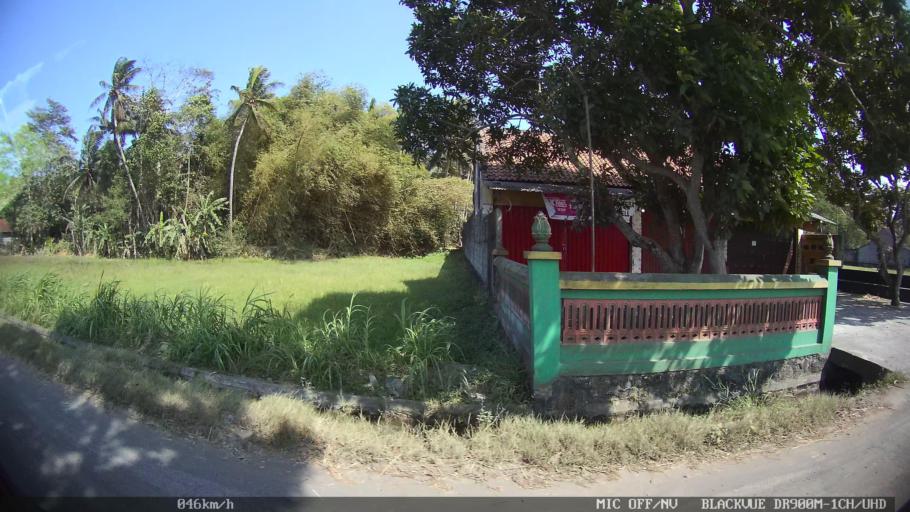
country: ID
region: Daerah Istimewa Yogyakarta
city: Srandakan
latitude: -7.9524
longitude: 110.2184
